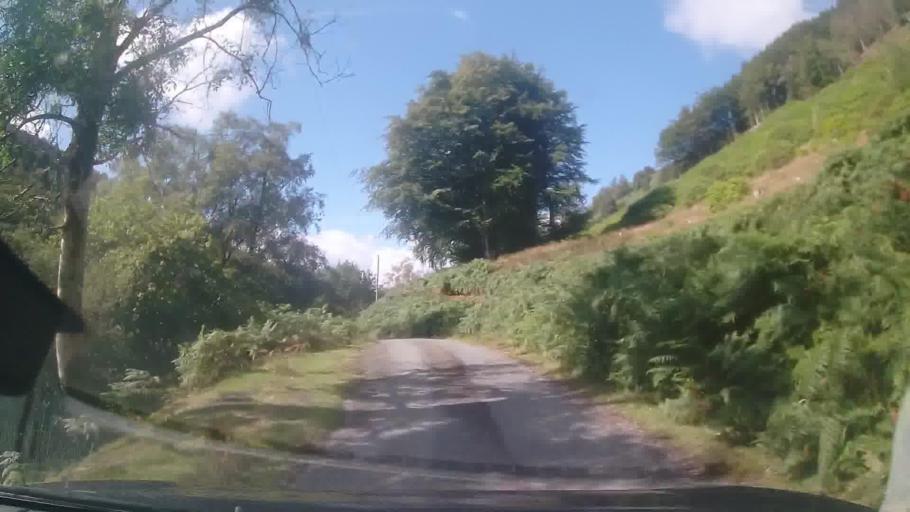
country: GB
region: Wales
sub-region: Gwynedd
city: Bala
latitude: 52.7916
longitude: -3.5514
